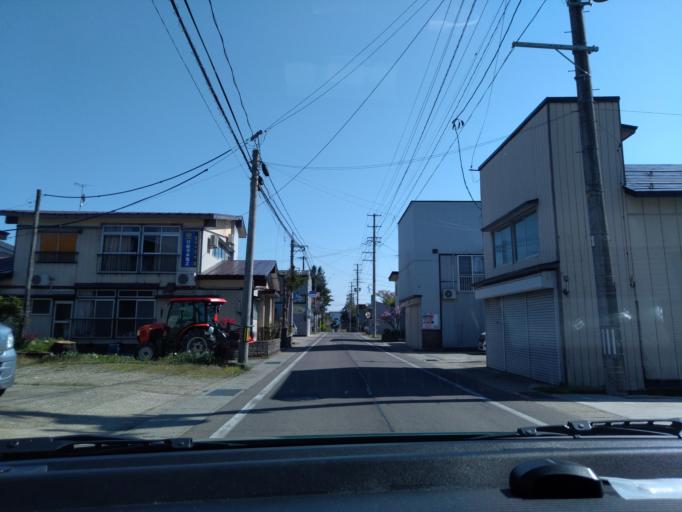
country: JP
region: Akita
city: Kakunodatemachi
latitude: 39.4994
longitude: 140.5943
